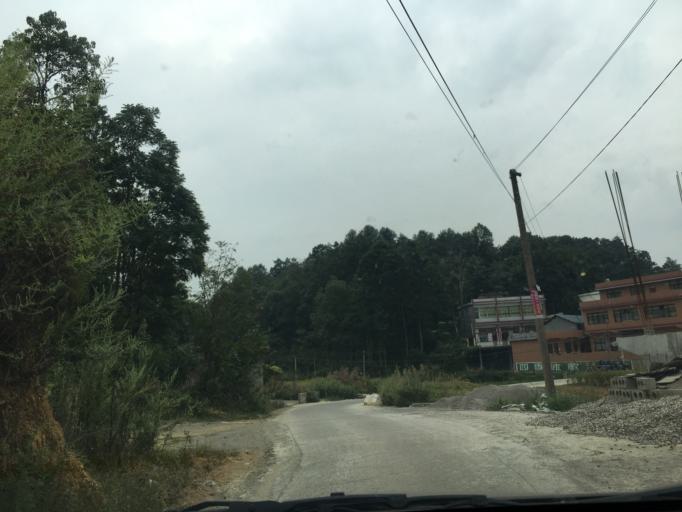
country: CN
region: Guangxi Zhuangzu Zizhiqu
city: Xinzhou
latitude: 25.5346
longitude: 105.6161
